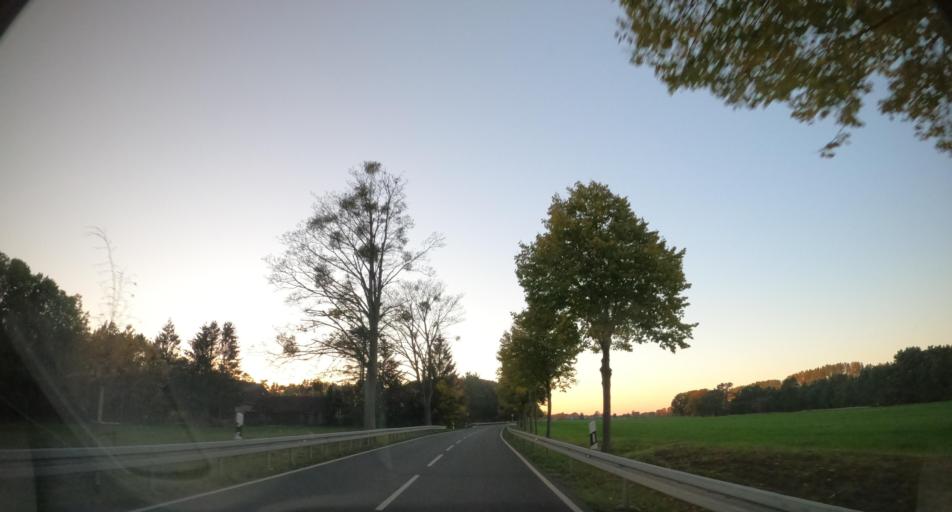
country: DE
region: Mecklenburg-Vorpommern
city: Ueckermunde
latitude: 53.7644
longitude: 13.9895
